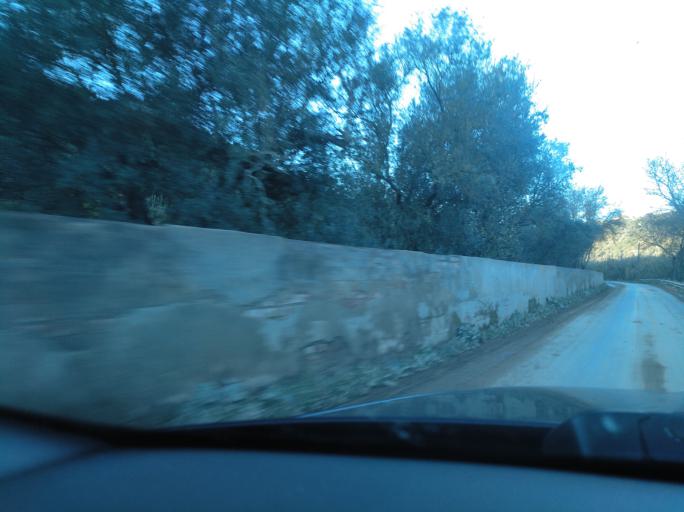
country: PT
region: Lisbon
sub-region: Loures
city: Bobadela
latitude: 38.8073
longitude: -9.1088
